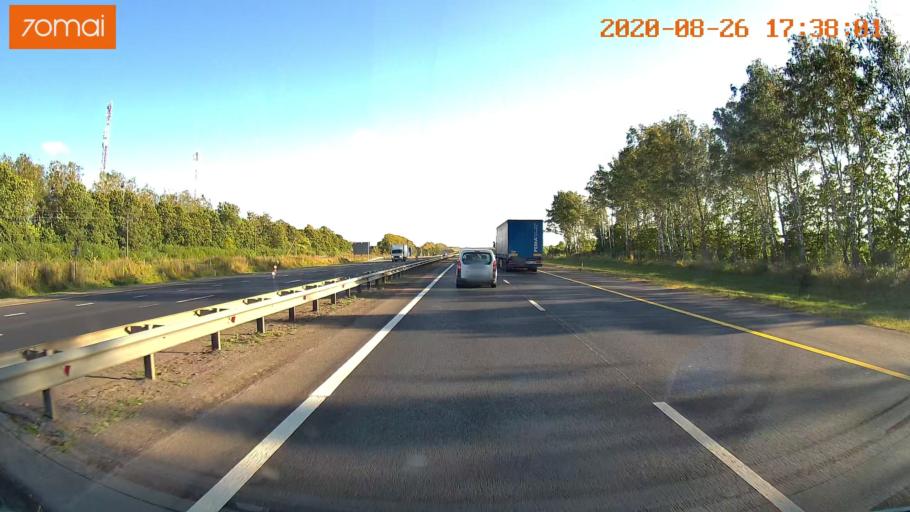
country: RU
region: Tula
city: Kazachka
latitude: 53.3496
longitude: 38.1815
